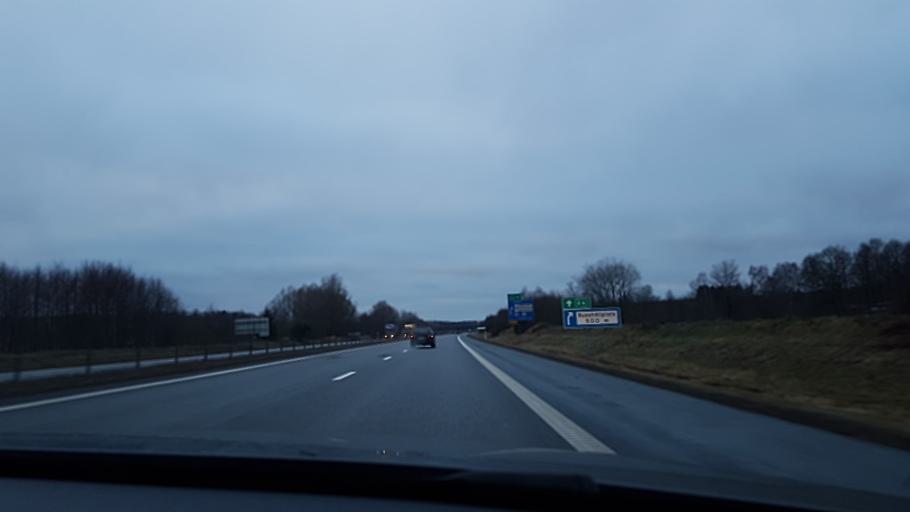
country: SE
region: Skane
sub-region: Orkelljunga Kommun
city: OErkelljunga
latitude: 56.2493
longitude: 13.2023
